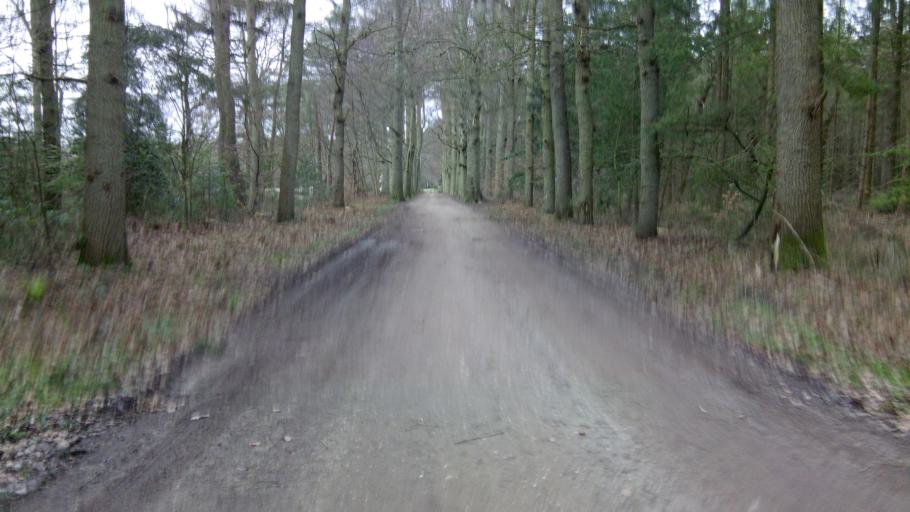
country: NL
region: Utrecht
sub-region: Gemeente Soest
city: Soest
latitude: 52.1768
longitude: 5.2474
